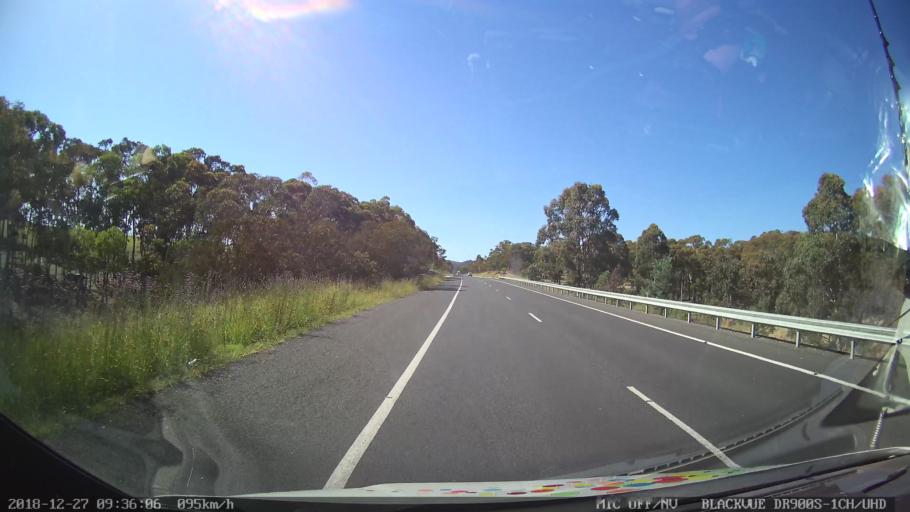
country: AU
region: New South Wales
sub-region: Lithgow
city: Portland
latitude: -33.2477
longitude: 150.0333
